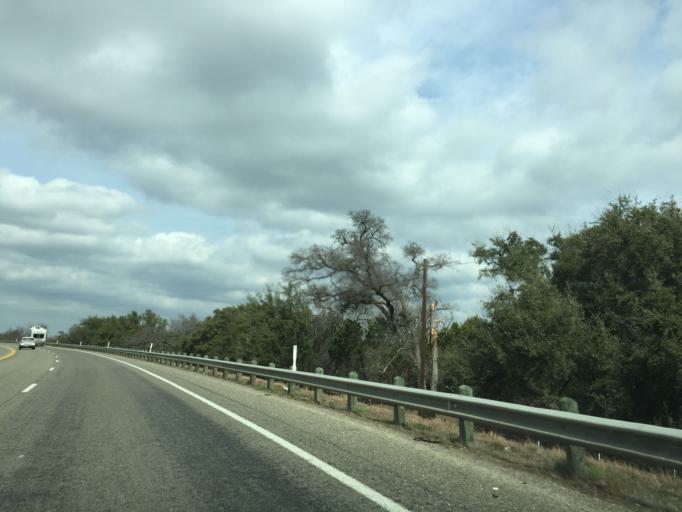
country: US
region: Texas
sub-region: Travis County
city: Briarcliff
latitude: 30.4505
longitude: -98.1487
